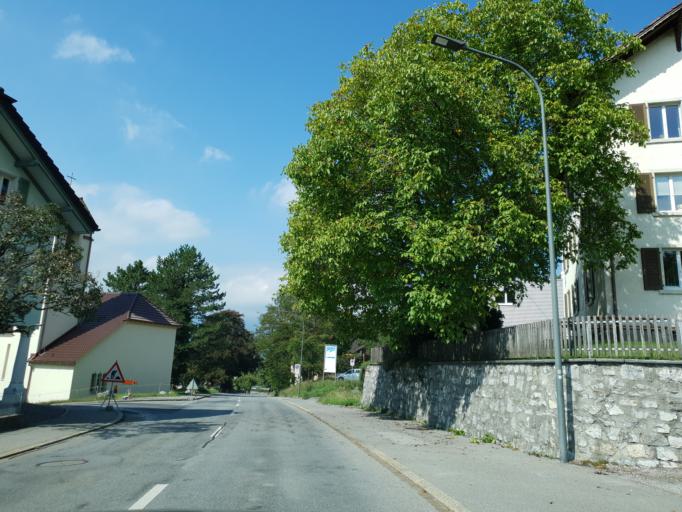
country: LI
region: Vaduz
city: Vaduz
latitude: 47.1502
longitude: 9.5145
